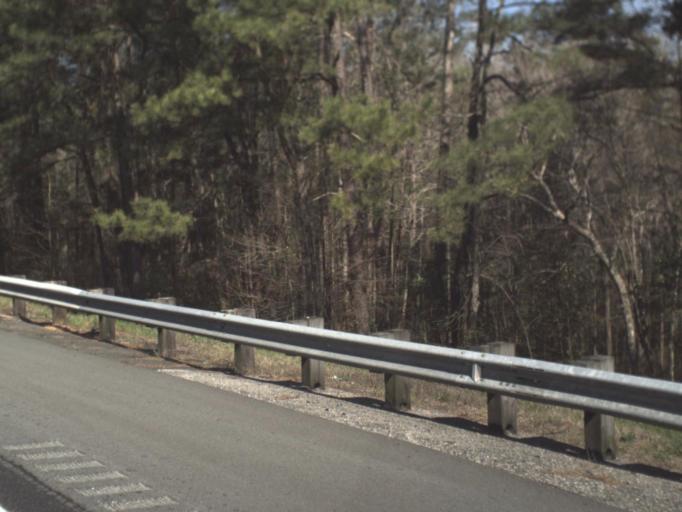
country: US
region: Florida
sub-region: Gadsden County
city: Gretna
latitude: 30.6183
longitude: -84.7695
